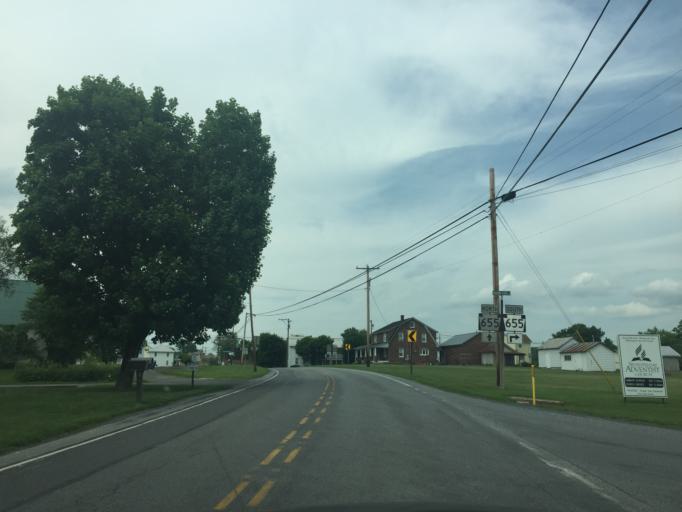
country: US
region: Maryland
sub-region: Washington County
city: Hancock
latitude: 39.8450
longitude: -78.1456
